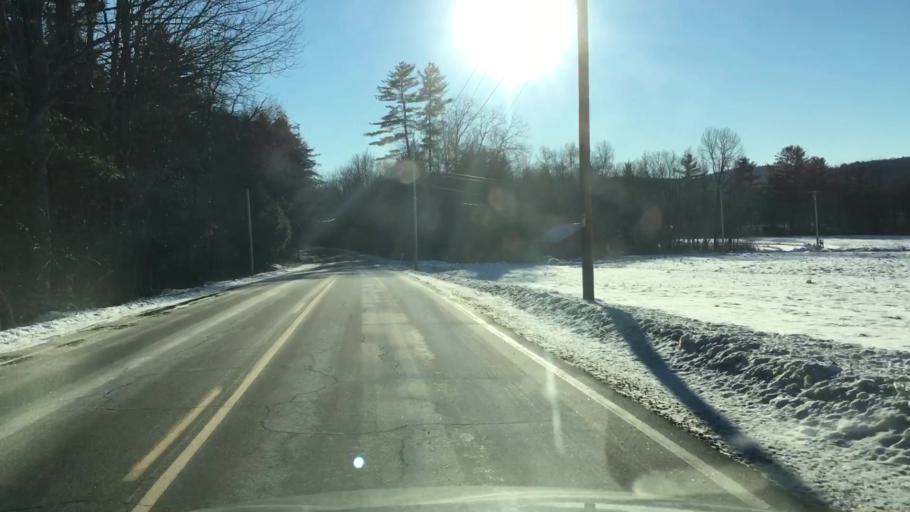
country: US
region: New Hampshire
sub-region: Grafton County
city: Woodsville
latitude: 44.2065
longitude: -72.0527
